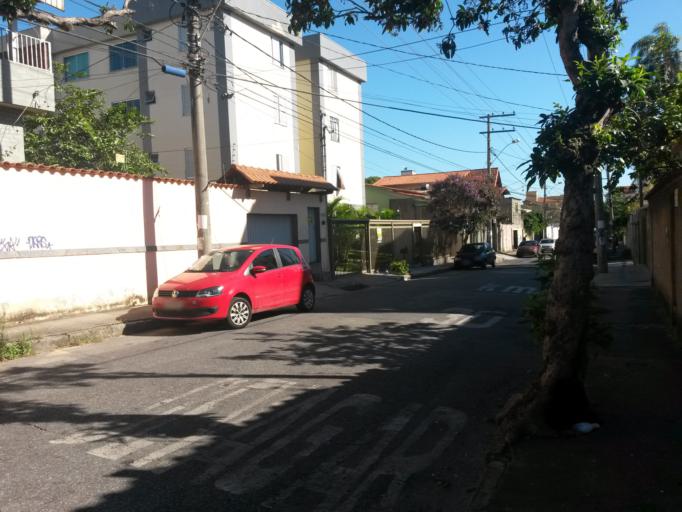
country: BR
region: Minas Gerais
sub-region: Belo Horizonte
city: Belo Horizonte
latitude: -19.9093
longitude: -43.9774
